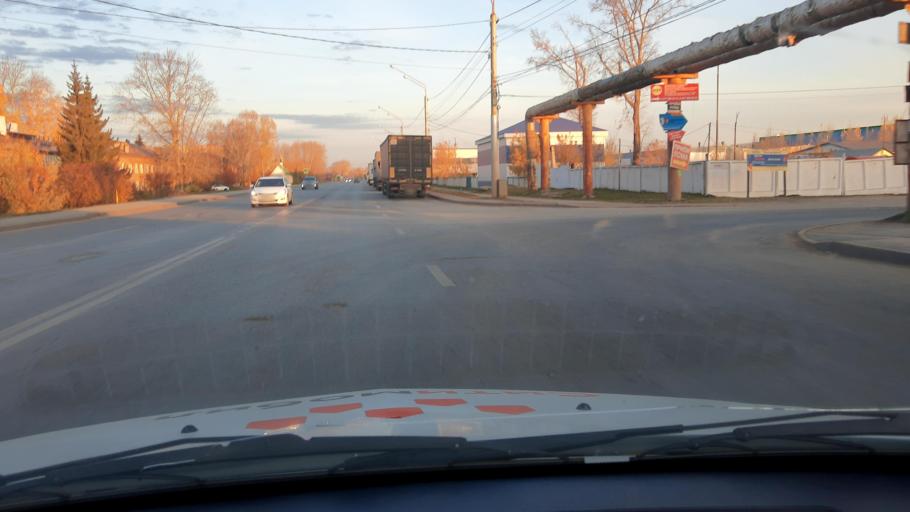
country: RU
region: Bashkortostan
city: Iglino
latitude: 54.7651
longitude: 56.2376
